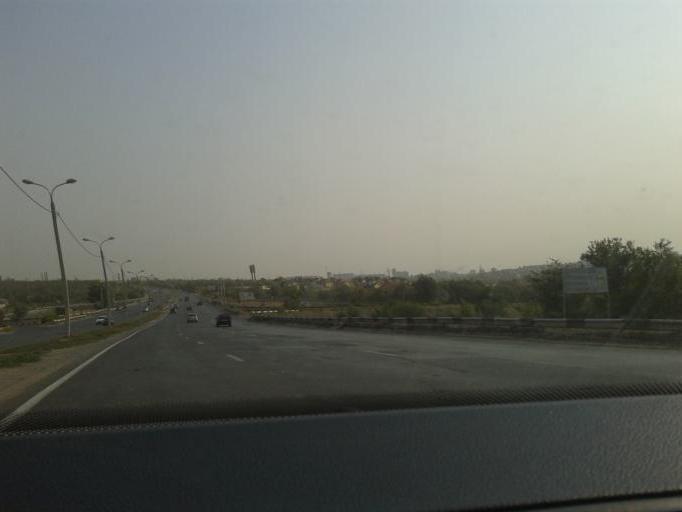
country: RU
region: Volgograd
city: Volgograd
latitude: 48.7296
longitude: 44.4505
